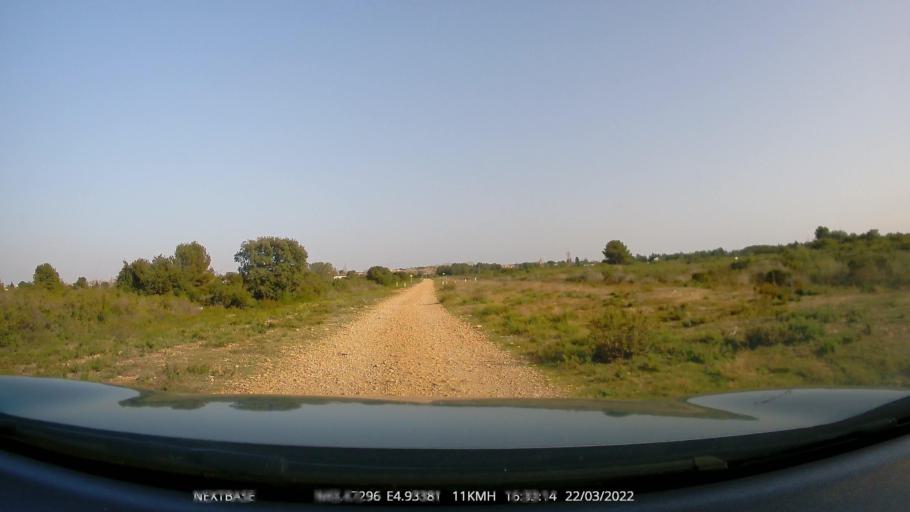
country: FR
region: Provence-Alpes-Cote d'Azur
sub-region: Departement des Bouches-du-Rhone
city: Fos-sur-Mer
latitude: 43.4730
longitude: 4.9337
